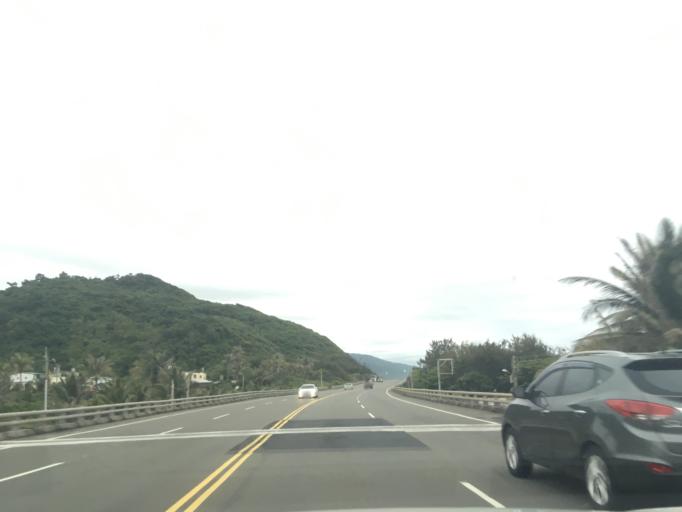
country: TW
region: Taiwan
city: Hengchun
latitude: 22.3072
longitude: 120.8900
